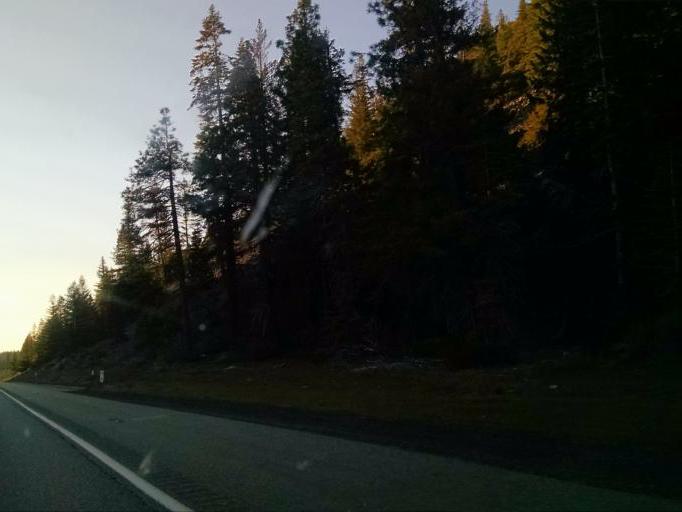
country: US
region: California
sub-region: Siskiyou County
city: Mount Shasta
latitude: 41.3583
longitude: -122.3597
